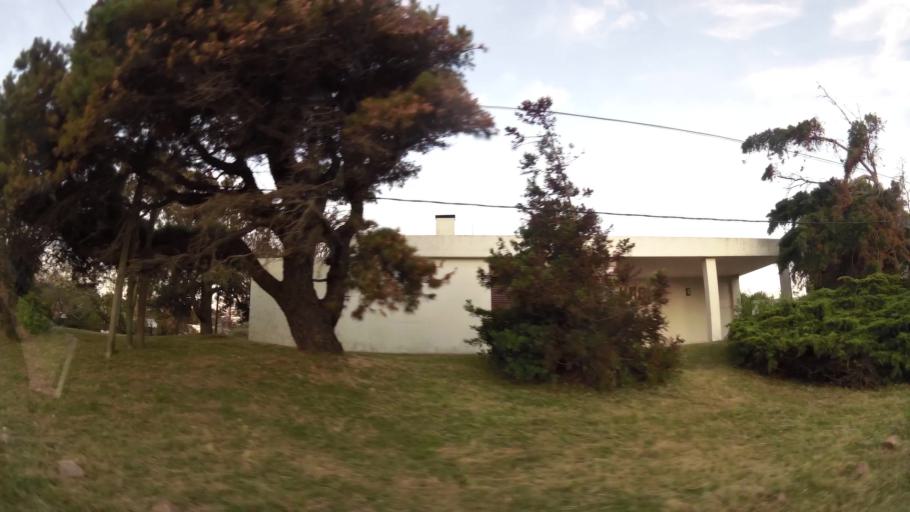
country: UY
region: Canelones
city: Atlantida
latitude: -34.7786
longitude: -55.7508
